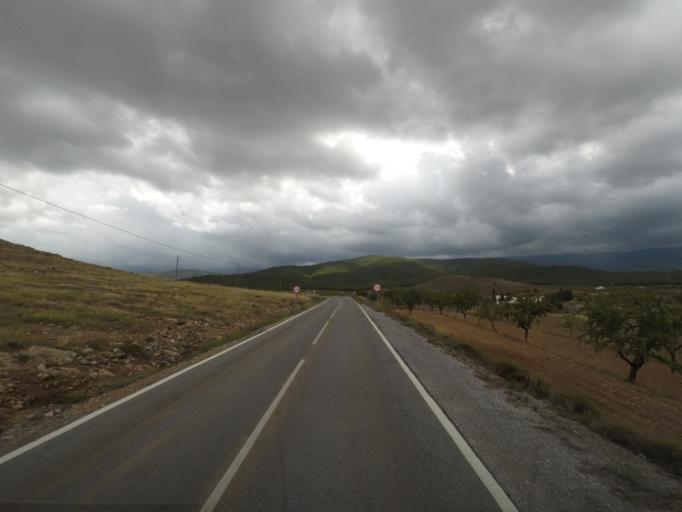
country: ES
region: Andalusia
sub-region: Provincia de Granada
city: Ferreira
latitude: 37.1804
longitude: -3.0583
